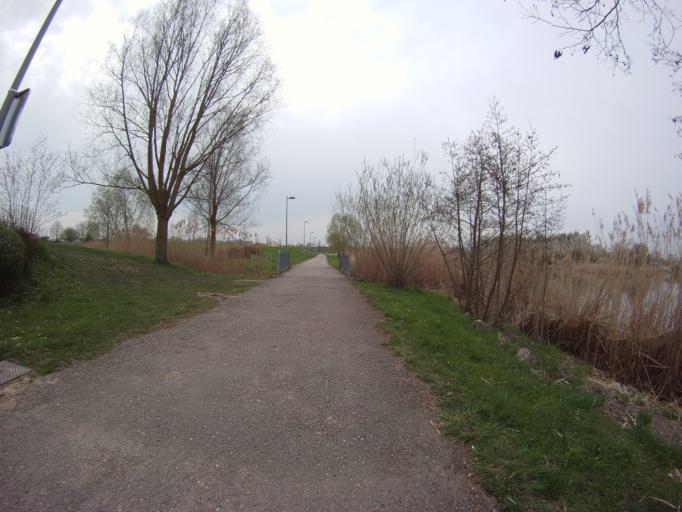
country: FR
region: Lorraine
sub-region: Departement de Meurthe-et-Moselle
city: Saint-Max
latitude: 48.6952
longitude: 6.2075
